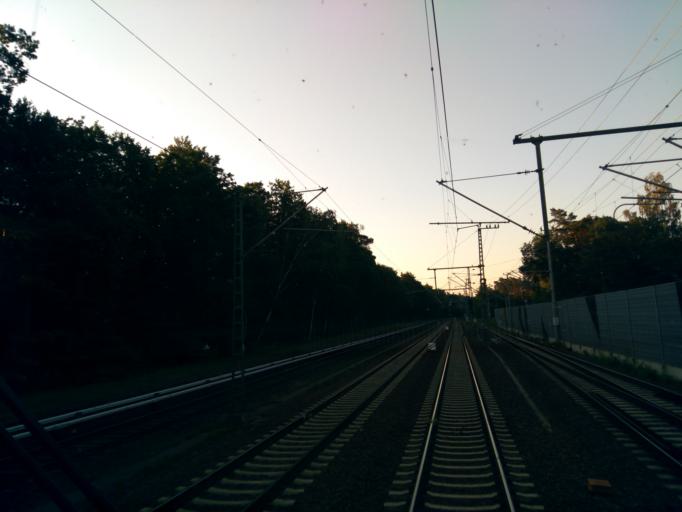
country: DE
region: Berlin
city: Bohnsdorf
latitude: 52.3989
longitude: 13.5942
